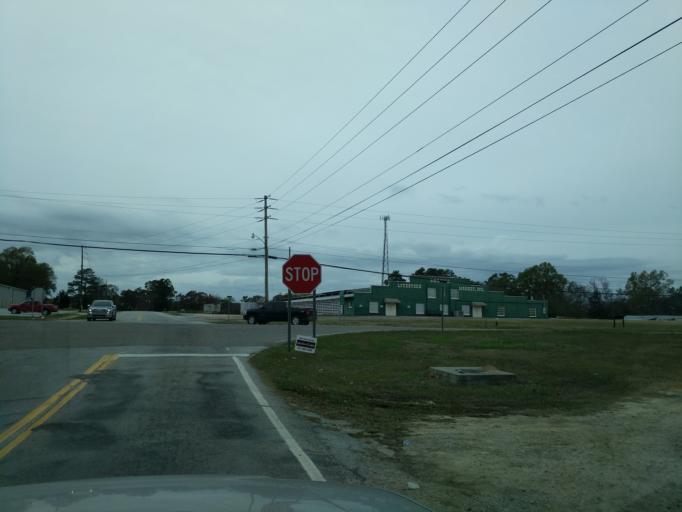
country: US
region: South Carolina
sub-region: Saluda County
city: Saluda
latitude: 34.0145
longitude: -81.7681
